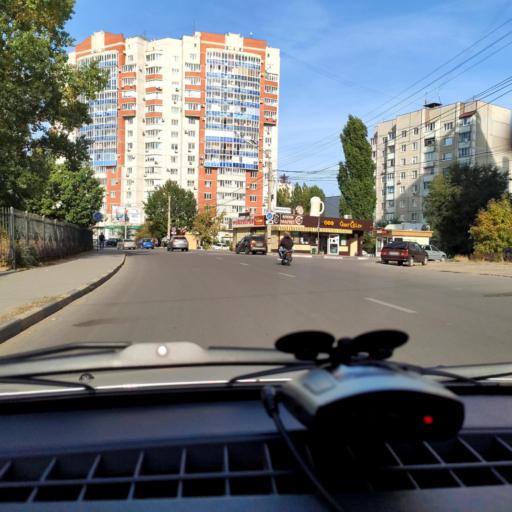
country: RU
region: Voronezj
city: Podgornoye
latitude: 51.7161
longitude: 39.1749
